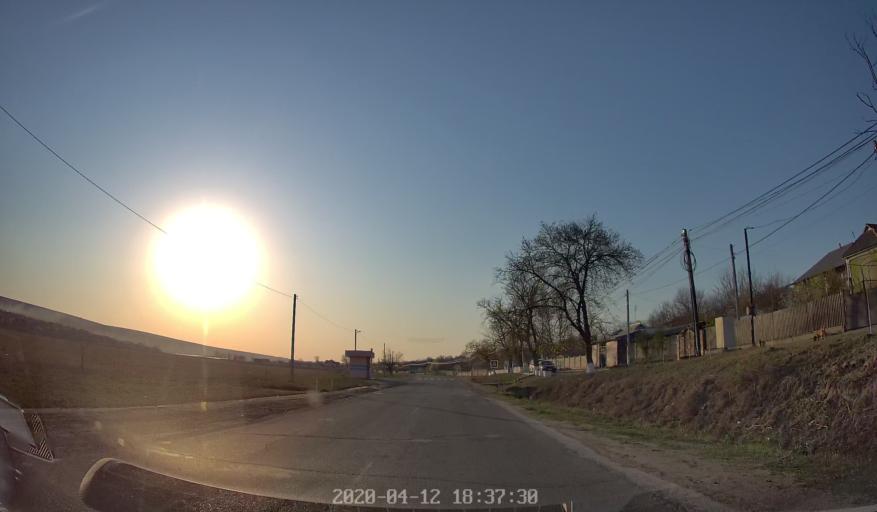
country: MD
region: Chisinau
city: Vadul lui Voda
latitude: 47.1214
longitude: 29.0142
